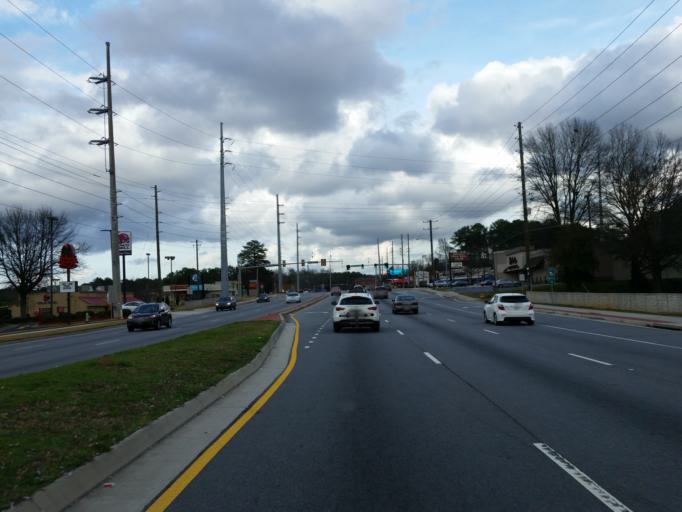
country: US
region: Georgia
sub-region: Cobb County
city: Marietta
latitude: 33.9682
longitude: -84.4899
